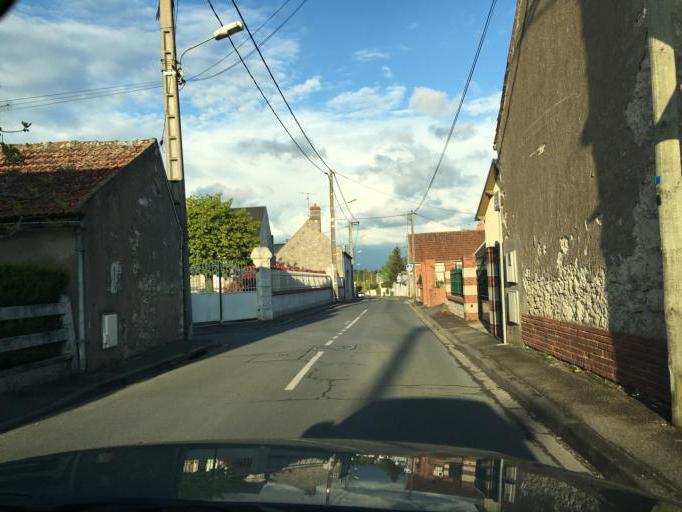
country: FR
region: Centre
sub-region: Departement du Loiret
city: Fleury-les-Aubrais
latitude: 47.9259
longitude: 1.9330
